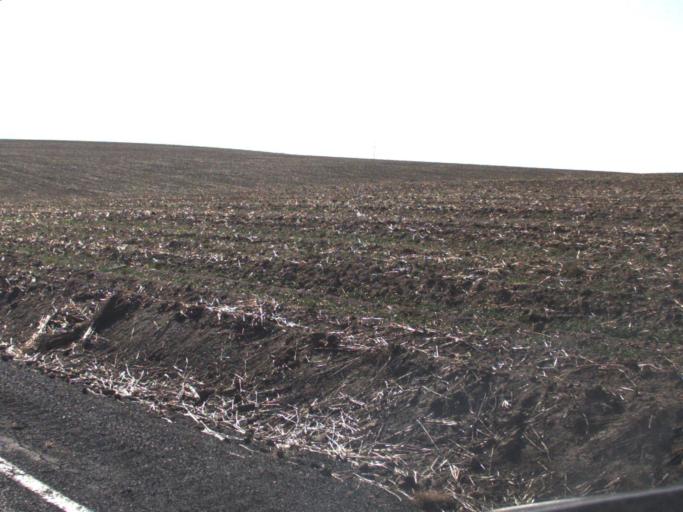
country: US
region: Washington
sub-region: Adams County
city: Ritzville
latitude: 47.0328
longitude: -118.6633
